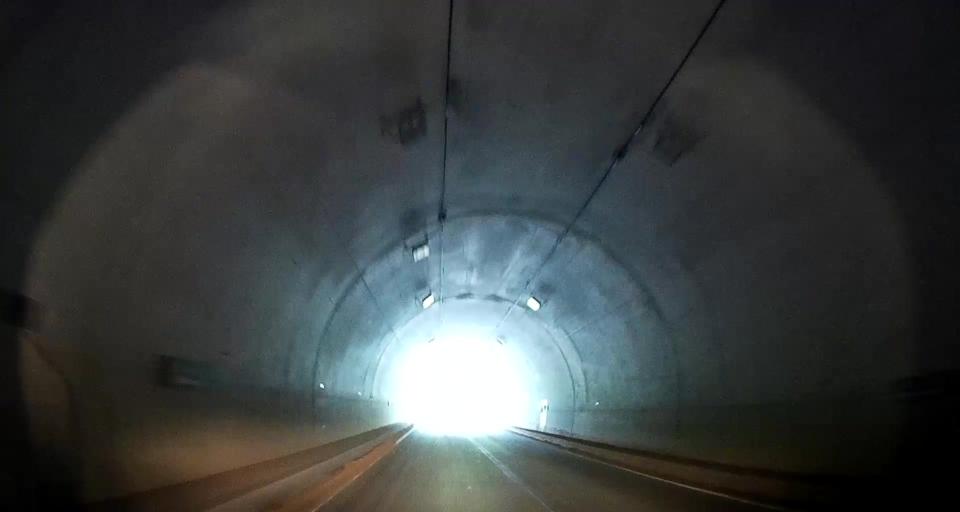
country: JP
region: Hokkaido
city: Chitose
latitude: 42.7887
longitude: 142.0461
